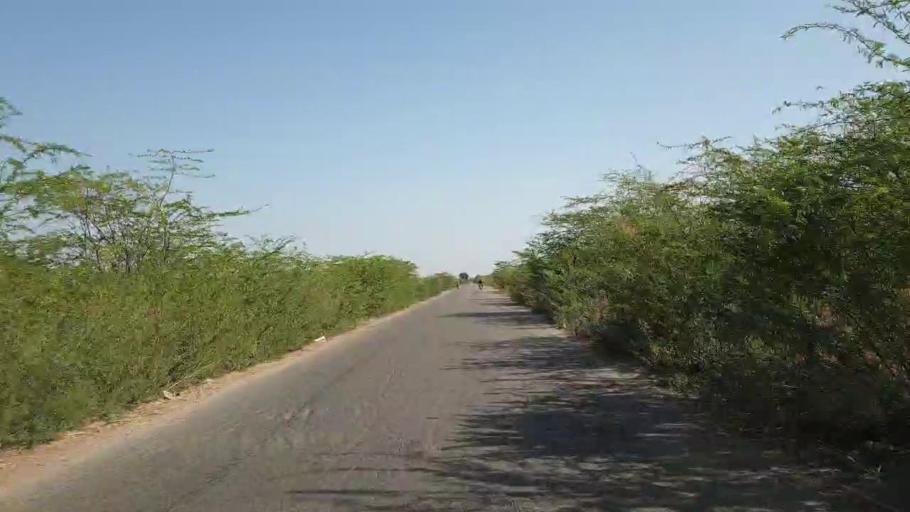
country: PK
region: Sindh
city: Chor
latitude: 25.4681
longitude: 69.7685
